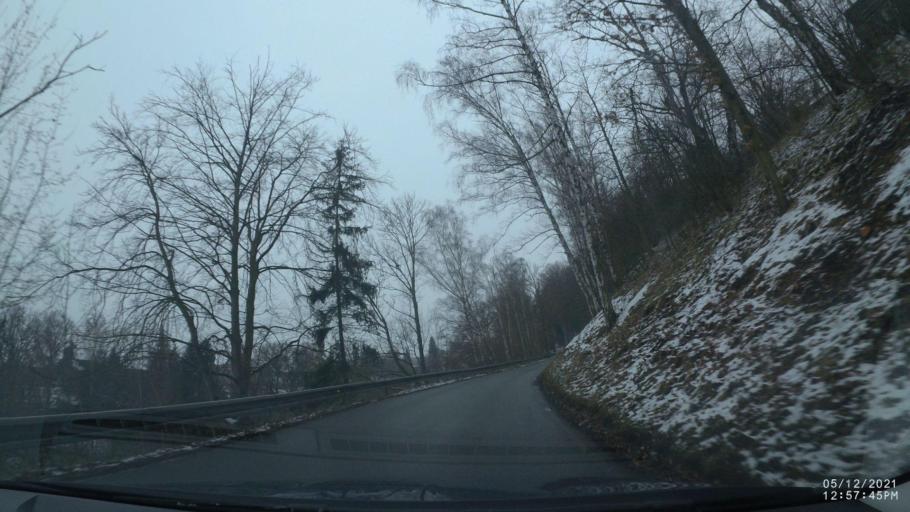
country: CZ
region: Kralovehradecky
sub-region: Okres Nachod
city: Nachod
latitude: 50.4147
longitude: 16.1547
